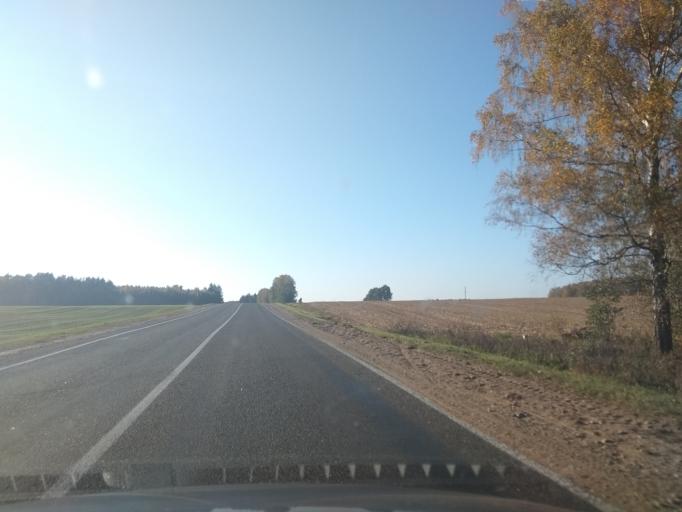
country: BY
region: Grodnenskaya
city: Vyalikaya Byerastavitsa
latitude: 53.1178
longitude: 24.0529
